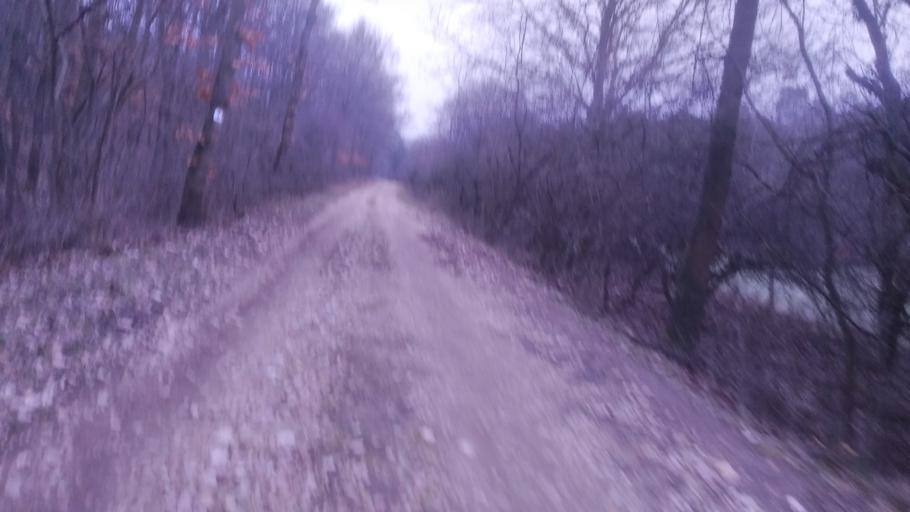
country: HU
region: Komarom-Esztergom
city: Dunaalmas
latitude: 47.7045
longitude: 18.3195
